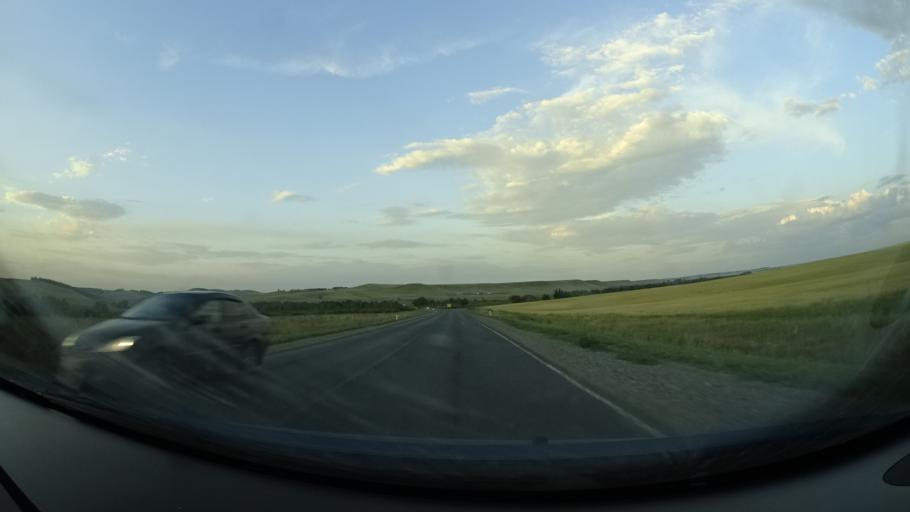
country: RU
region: Orenburg
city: Severnoye
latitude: 54.1306
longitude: 52.5841
